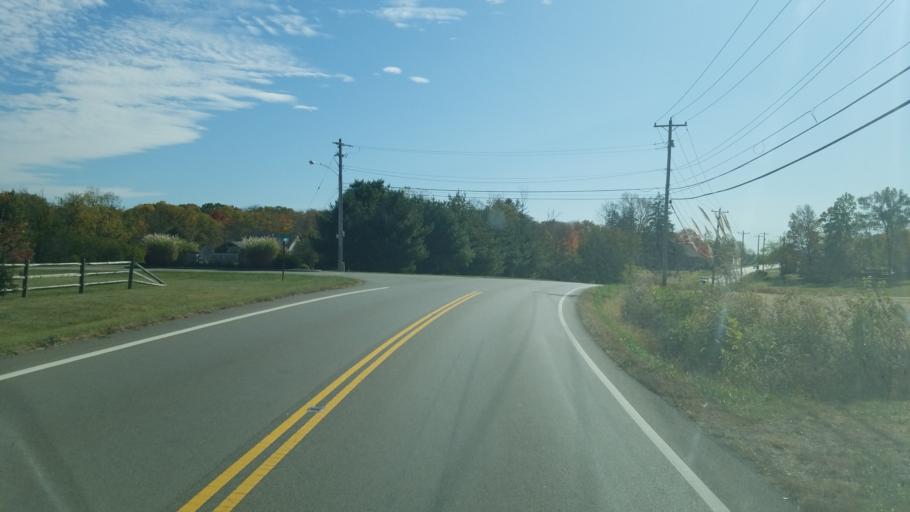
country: US
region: Ohio
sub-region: Warren County
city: Lebanon
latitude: 39.4182
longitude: -84.1579
